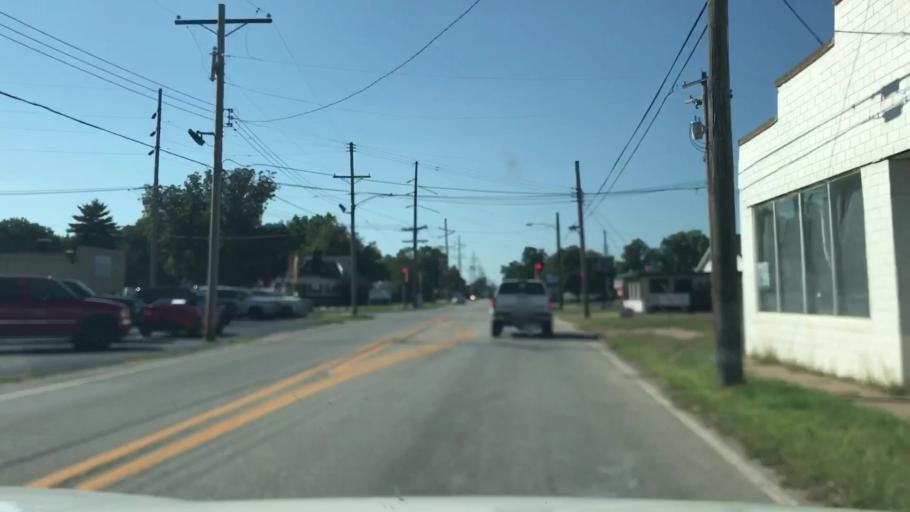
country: US
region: Illinois
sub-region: Madison County
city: Wood River
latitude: 38.8673
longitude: -90.0861
